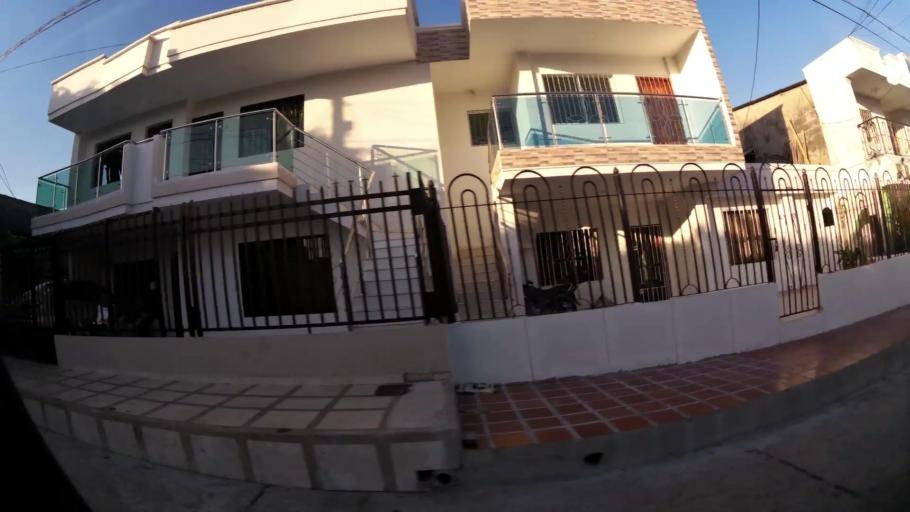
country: CO
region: Atlantico
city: Barranquilla
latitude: 10.9705
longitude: -74.8075
